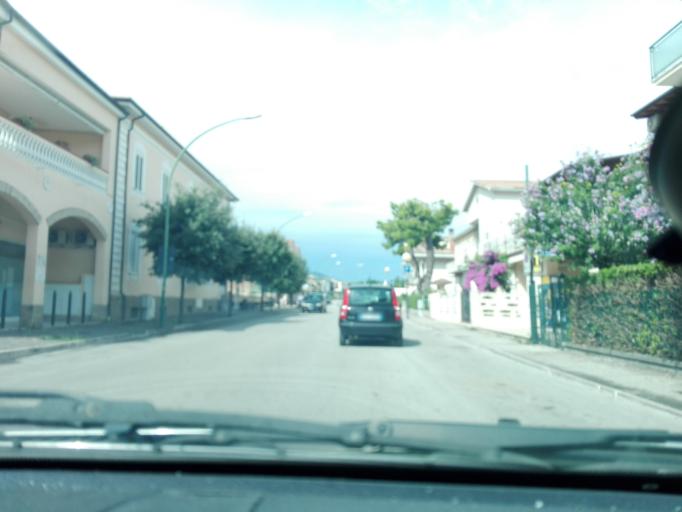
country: IT
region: Abruzzo
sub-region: Provincia di Teramo
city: Pineto
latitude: 42.6106
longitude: 14.0648
